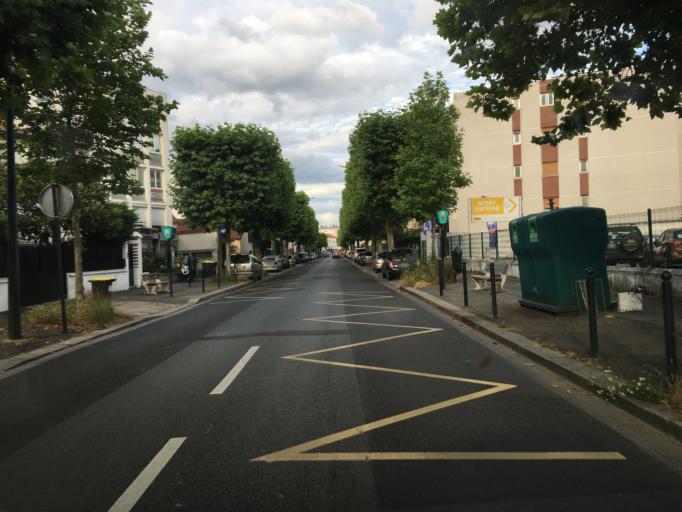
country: FR
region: Ile-de-France
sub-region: Departement du Val-de-Marne
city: Saint-Maur-des-Fosses
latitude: 48.7978
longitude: 2.4988
